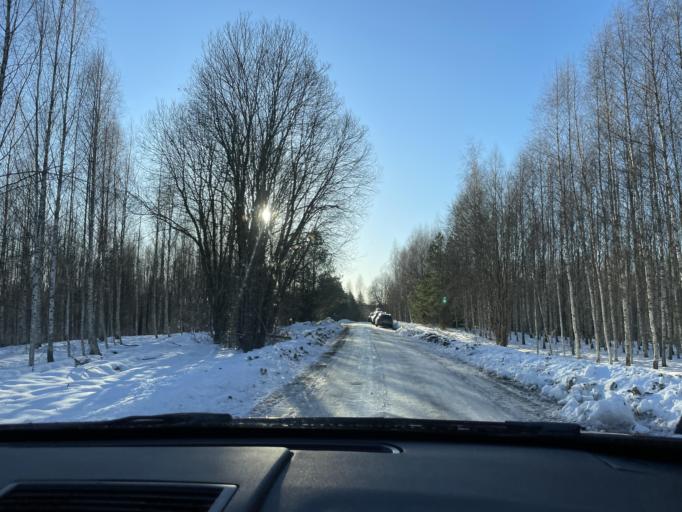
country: LV
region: Ludzas Rajons
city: Ludza
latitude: 56.4516
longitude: 27.6348
